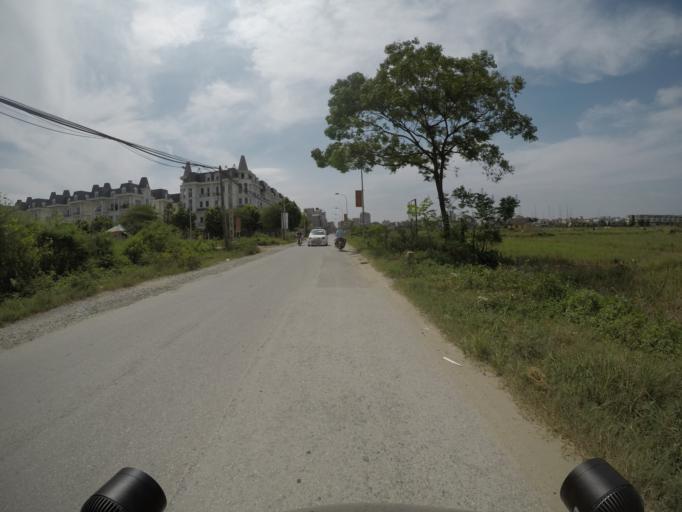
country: VN
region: Ha Noi
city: Troi
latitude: 21.0746
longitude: 105.7094
